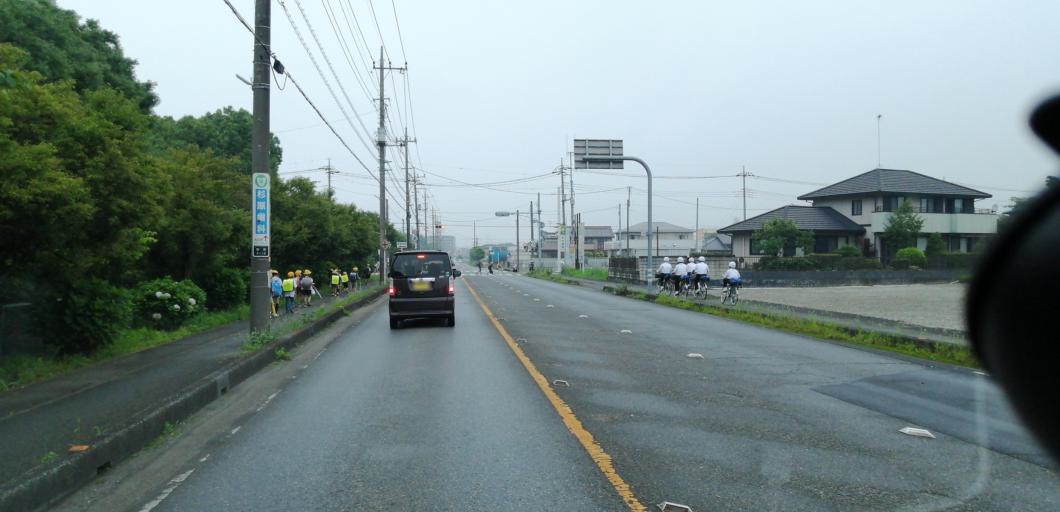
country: JP
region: Saitama
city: Kukichuo
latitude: 36.0880
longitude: 139.6875
